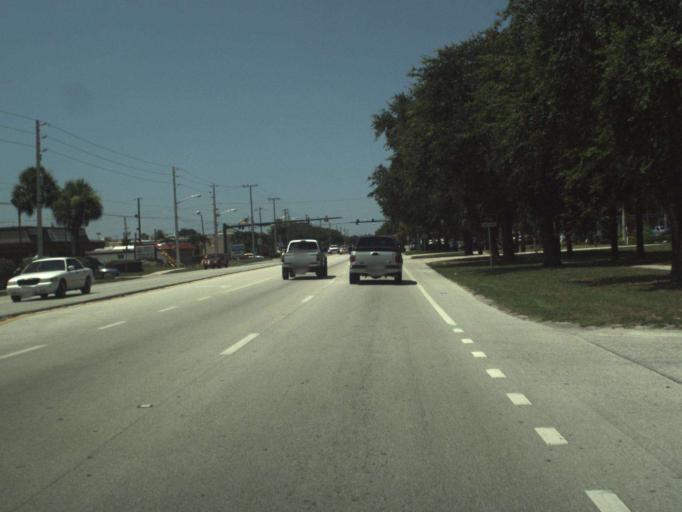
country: US
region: Florida
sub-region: Saint Lucie County
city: Fort Pierce
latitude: 27.4194
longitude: -80.3258
